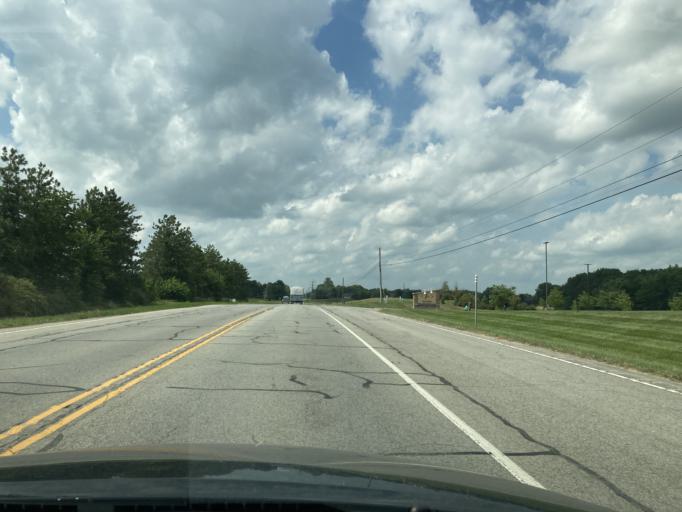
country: US
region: Indiana
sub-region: Boone County
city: Zionsville
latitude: 39.9857
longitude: -86.2584
